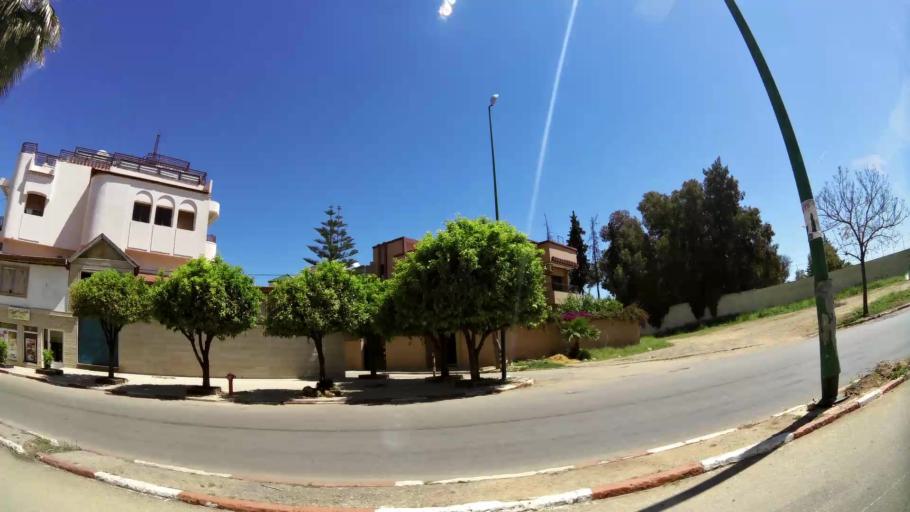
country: MA
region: Meknes-Tafilalet
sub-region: Meknes
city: Meknes
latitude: 33.9002
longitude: -5.5141
